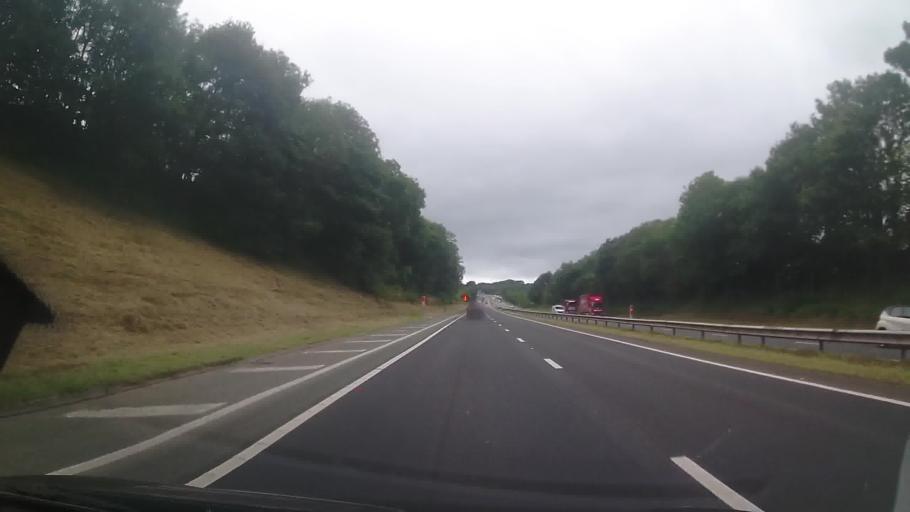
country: GB
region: Wales
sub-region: Gwynedd
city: Bethesda
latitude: 53.2110
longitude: -4.0888
